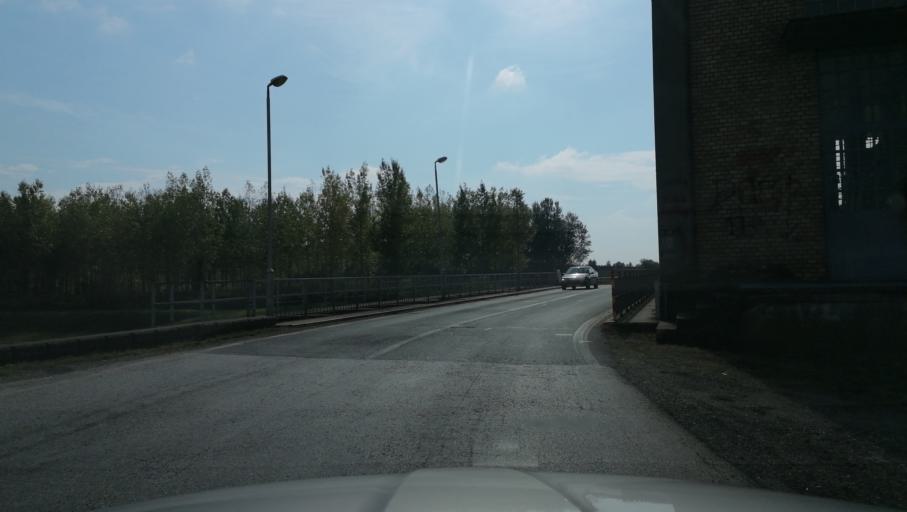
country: RS
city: Bosut
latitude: 44.9437
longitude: 19.3684
